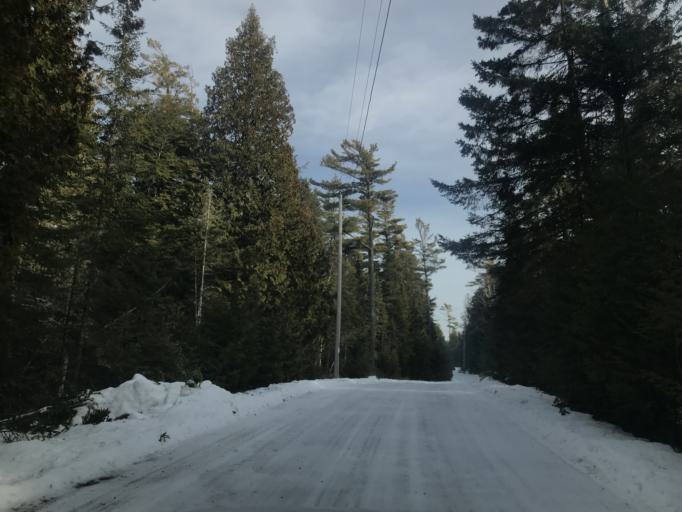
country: US
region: Wisconsin
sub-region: Door County
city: Sturgeon Bay
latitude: 45.1418
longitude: -87.0408
